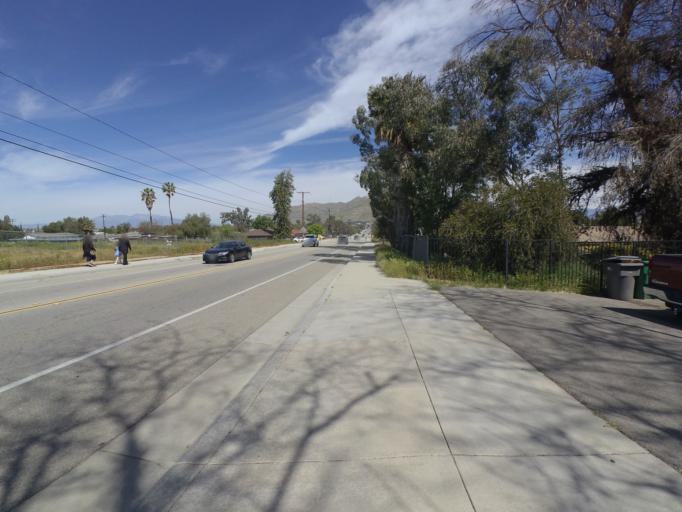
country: US
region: California
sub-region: Riverside County
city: March Air Force Base
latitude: 33.9209
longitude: -117.2787
